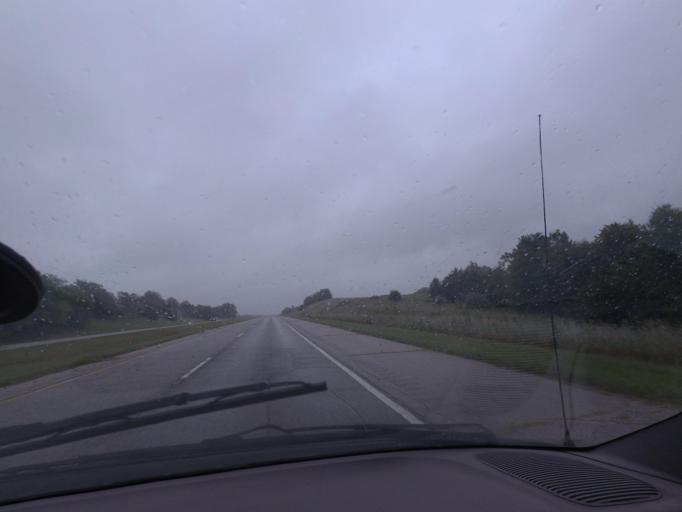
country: US
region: Illinois
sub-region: Pike County
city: Pittsfield
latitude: 39.6881
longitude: -90.9011
